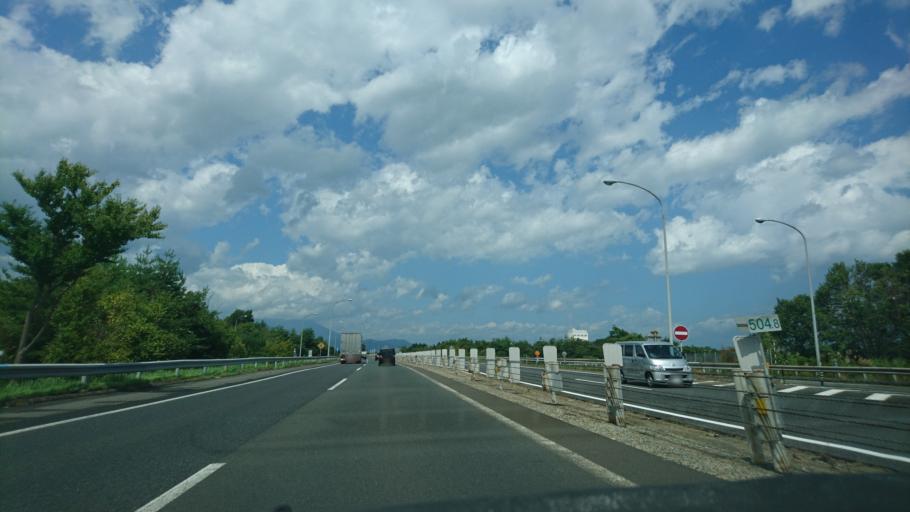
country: JP
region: Iwate
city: Morioka-shi
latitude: 39.6504
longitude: 141.1235
